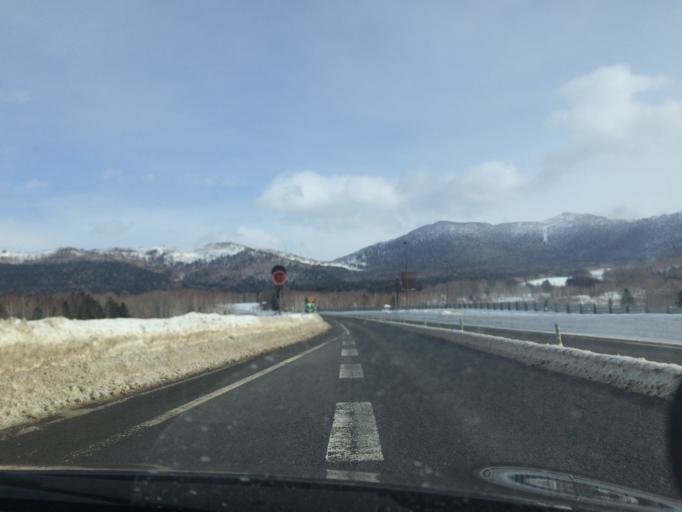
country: JP
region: Hokkaido
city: Shimo-furano
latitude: 43.0433
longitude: 142.6638
